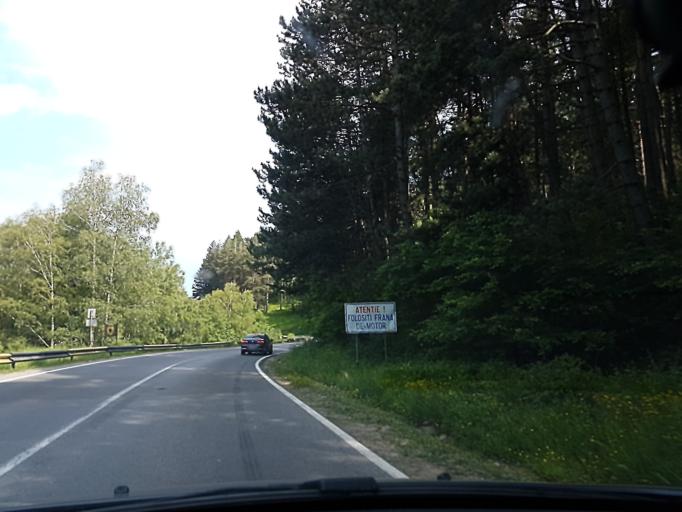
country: RO
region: Prahova
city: Maneciu
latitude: 45.3303
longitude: 25.9742
